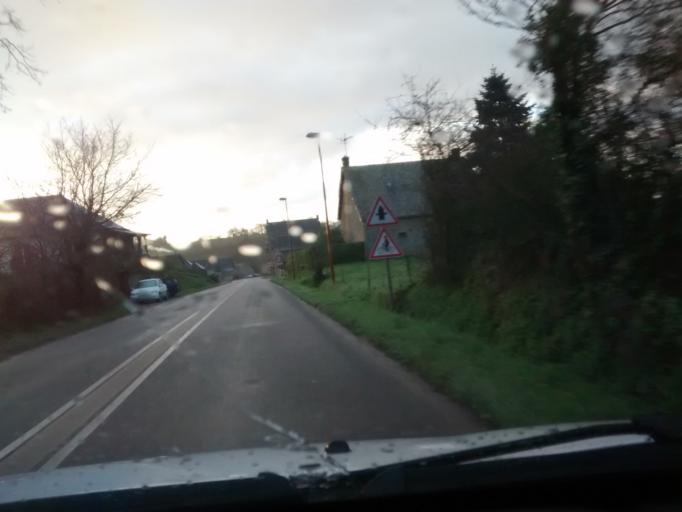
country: FR
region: Brittany
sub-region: Departement d'Ille-et-Vilaine
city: Domalain
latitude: 47.9671
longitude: -1.2661
